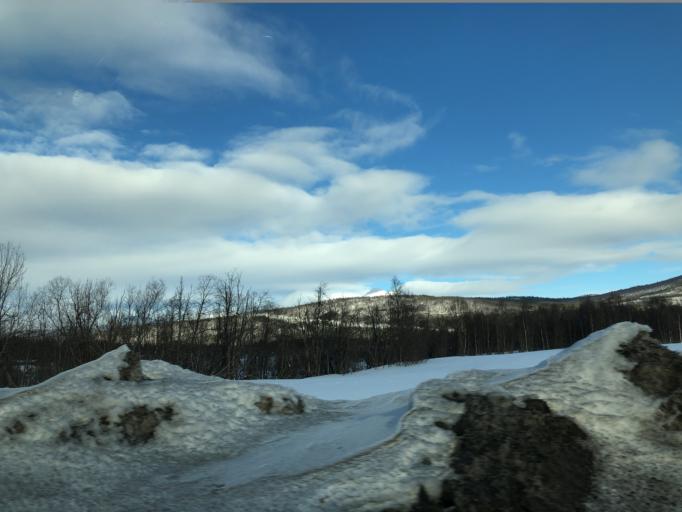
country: NO
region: Troms
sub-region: Malselv
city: Moen
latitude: 69.1202
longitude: 18.5798
